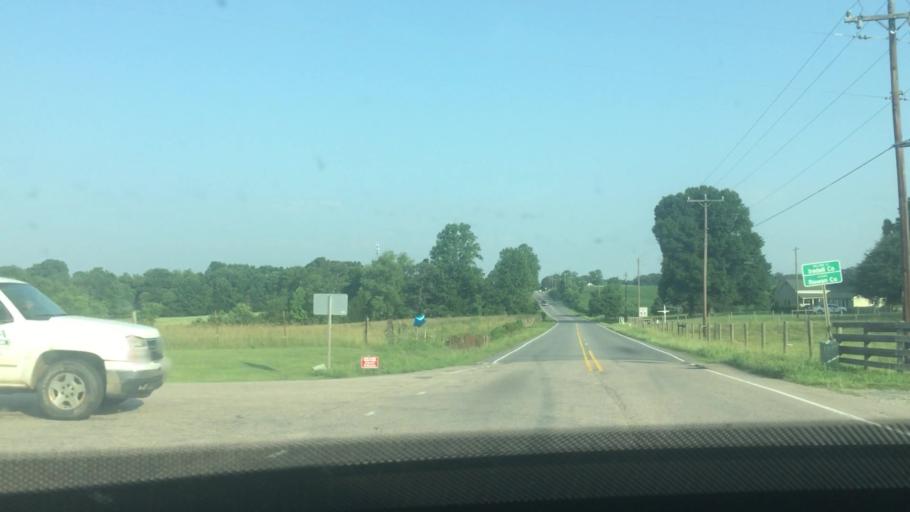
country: US
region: North Carolina
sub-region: Iredell County
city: Mooresville
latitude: 35.5893
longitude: -80.7507
